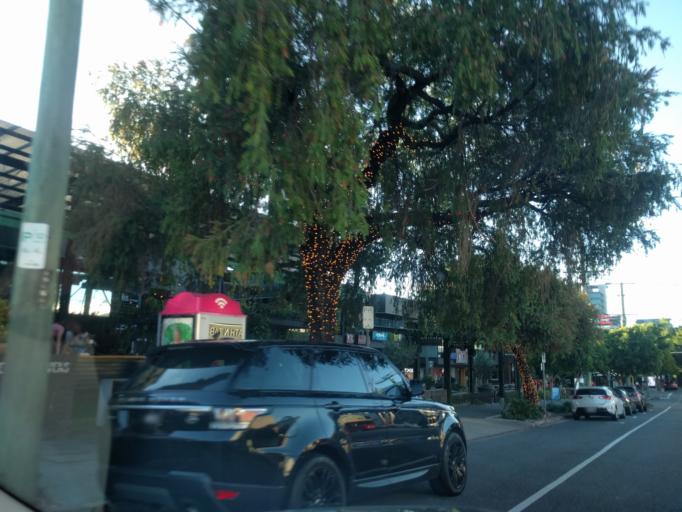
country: AU
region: Queensland
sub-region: Brisbane
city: Fortitude Valley
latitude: -27.4576
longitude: 153.0410
